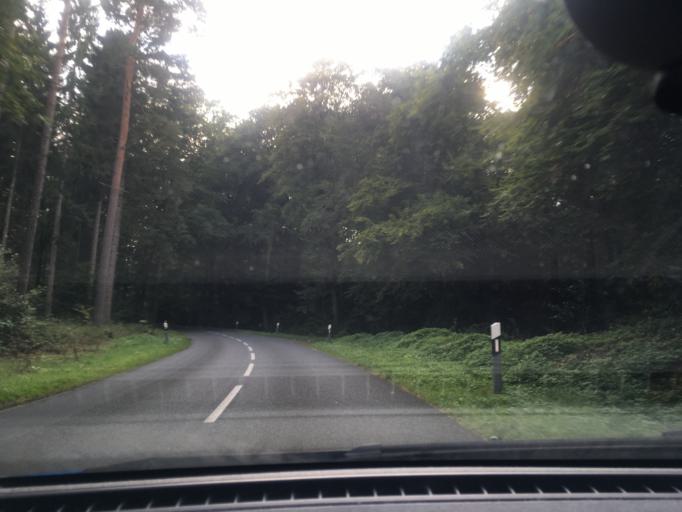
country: DE
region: Lower Saxony
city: Reinstorf
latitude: 53.2188
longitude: 10.5614
